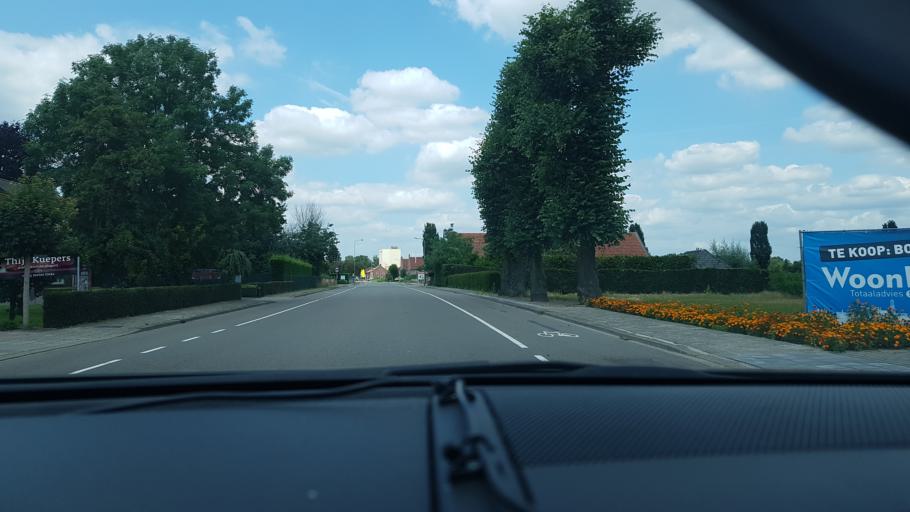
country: NL
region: Limburg
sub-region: Gemeente Nederweert
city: Nederweert
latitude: 51.2757
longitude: 5.7745
